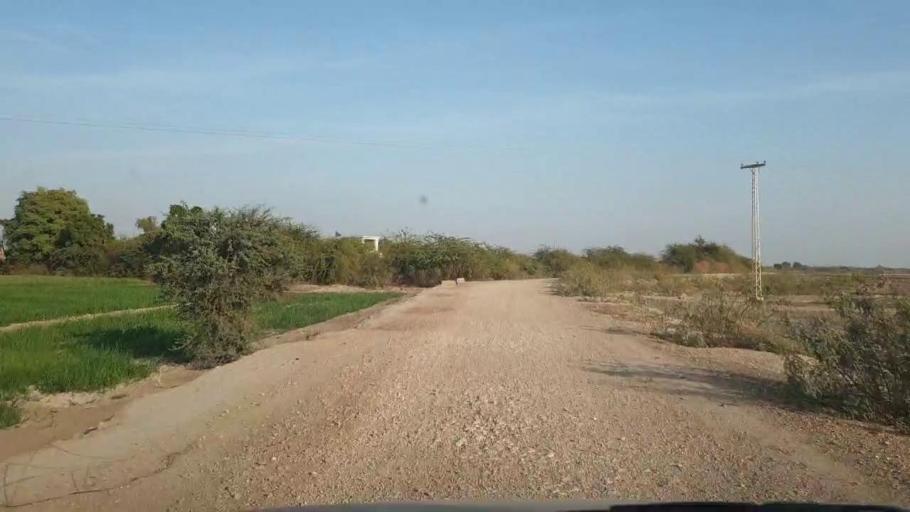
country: PK
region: Sindh
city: Chambar
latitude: 25.2384
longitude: 68.8031
